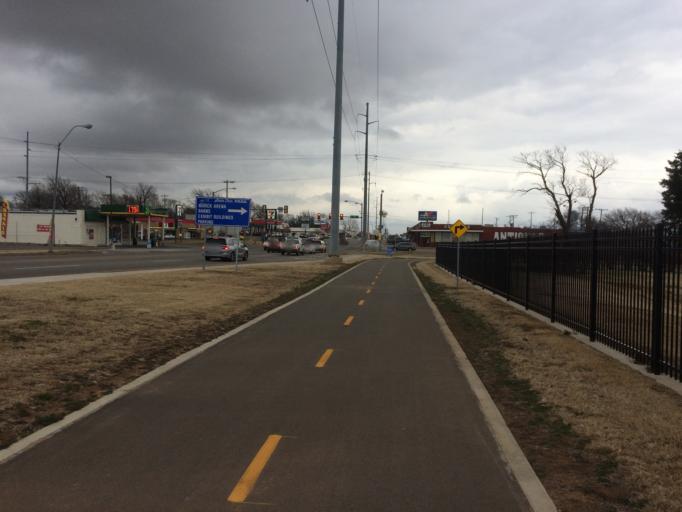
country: US
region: Oklahoma
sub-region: Oklahoma County
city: Oklahoma City
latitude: 35.4785
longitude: -97.5669
